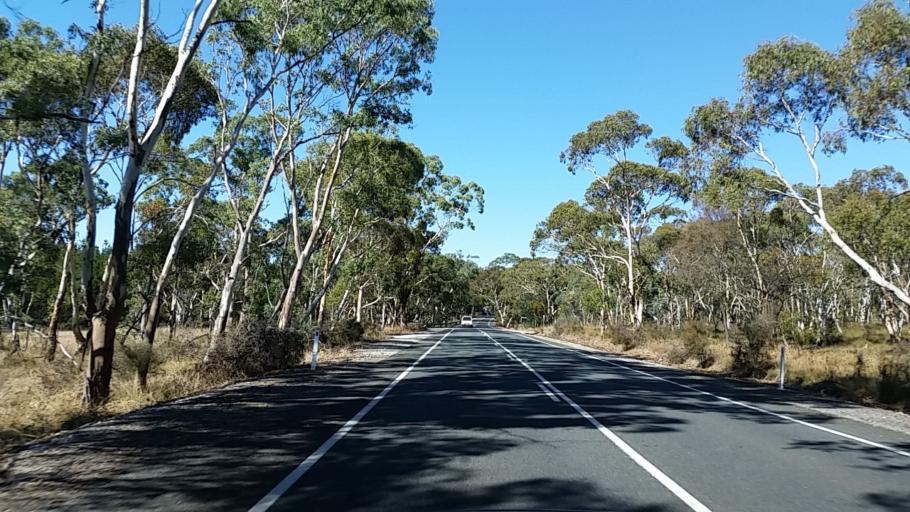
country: AU
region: South Australia
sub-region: Adelaide Hills
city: Birdwood
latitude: -34.7507
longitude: 138.9917
